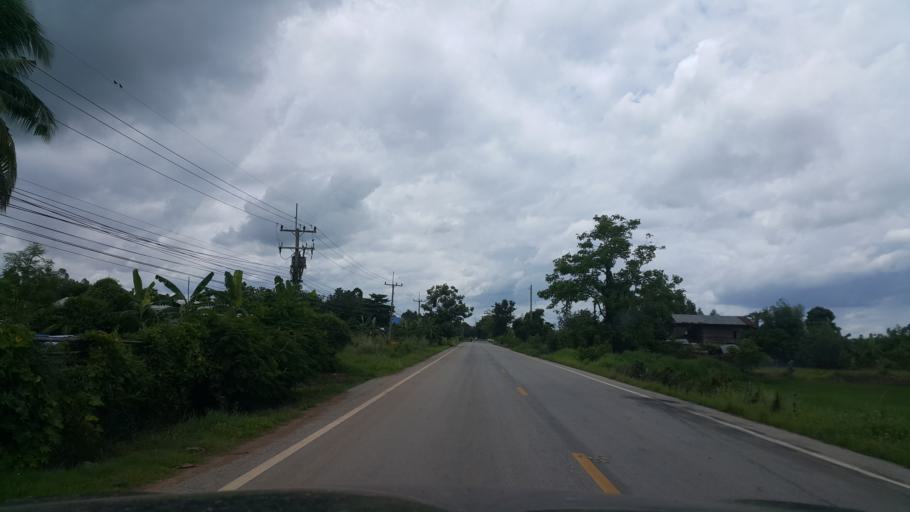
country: TH
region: Sukhothai
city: Kong Krailat
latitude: 16.9115
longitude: 99.8773
